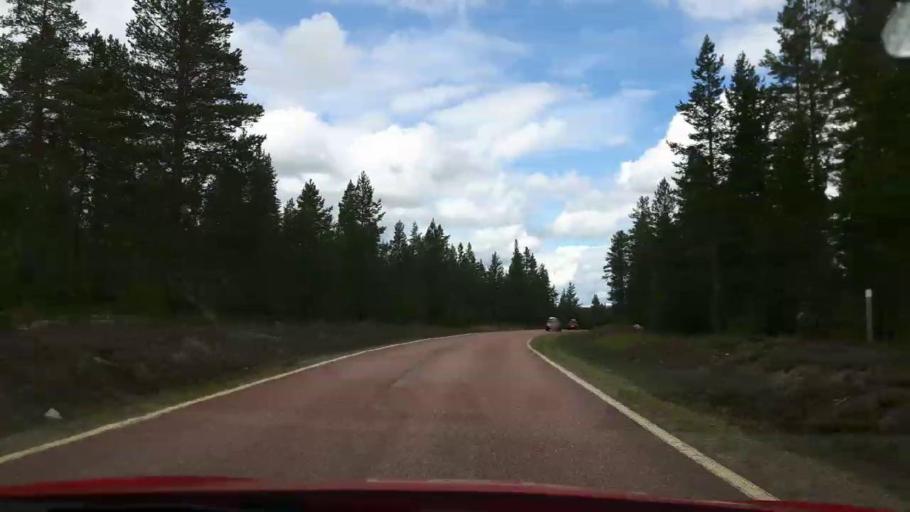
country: NO
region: Hedmark
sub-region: Trysil
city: Innbygda
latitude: 61.8567
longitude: 12.9474
